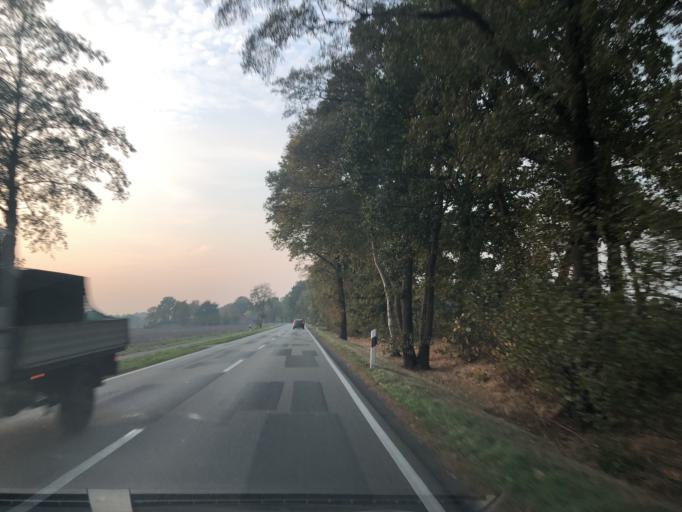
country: DE
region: Lower Saxony
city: Bosel
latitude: 52.9999
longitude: 7.9917
